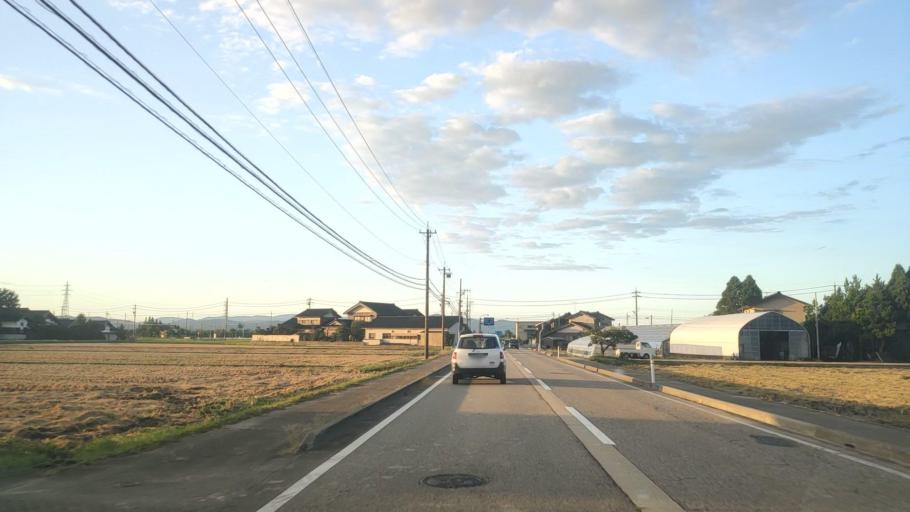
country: JP
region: Toyama
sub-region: Oyabe Shi
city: Oyabe
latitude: 36.6239
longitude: 136.8886
